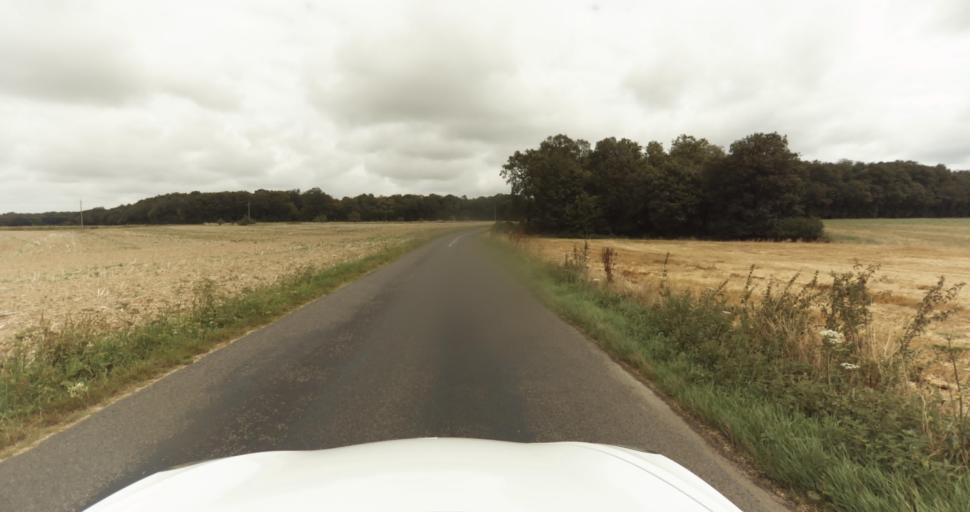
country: FR
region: Haute-Normandie
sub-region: Departement de l'Eure
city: Claville
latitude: 49.0326
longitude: 1.0542
